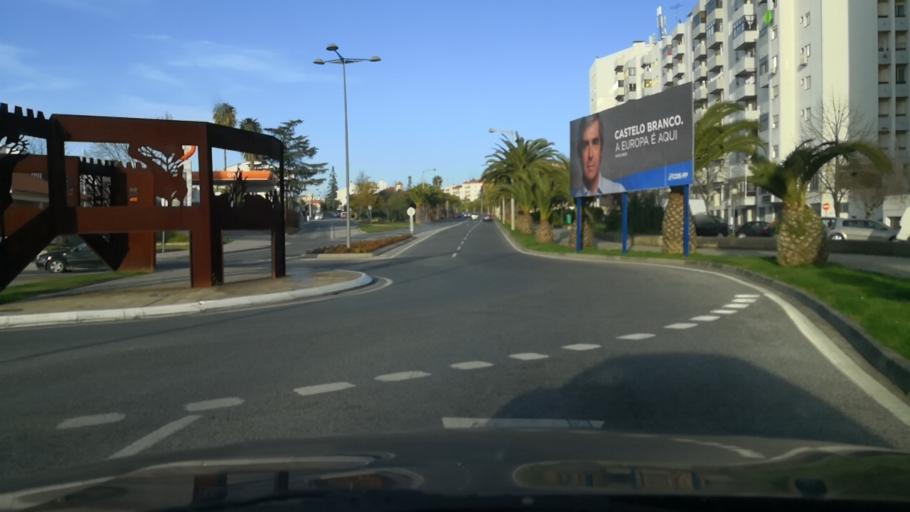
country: PT
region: Castelo Branco
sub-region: Castelo Branco
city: Castelo Branco
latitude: 39.8159
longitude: -7.5020
